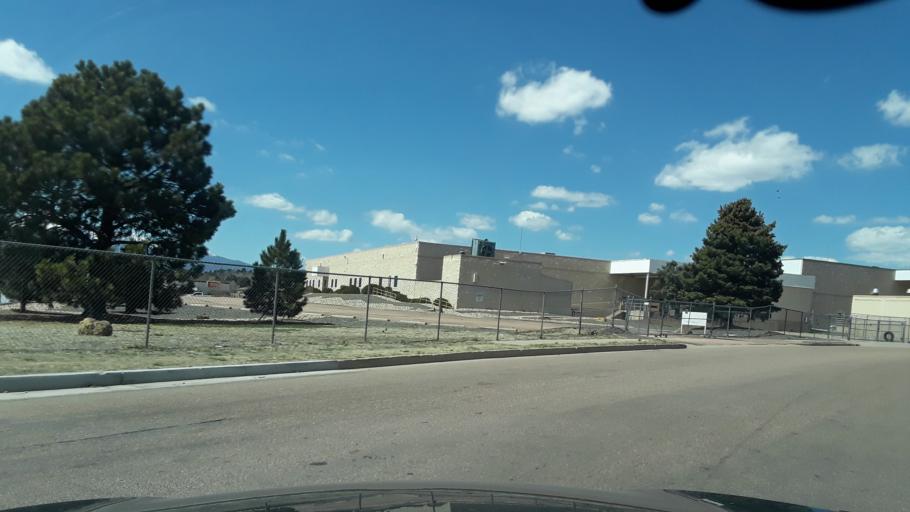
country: US
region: Colorado
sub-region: El Paso County
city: Cimarron Hills
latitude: 38.8670
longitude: -104.7181
